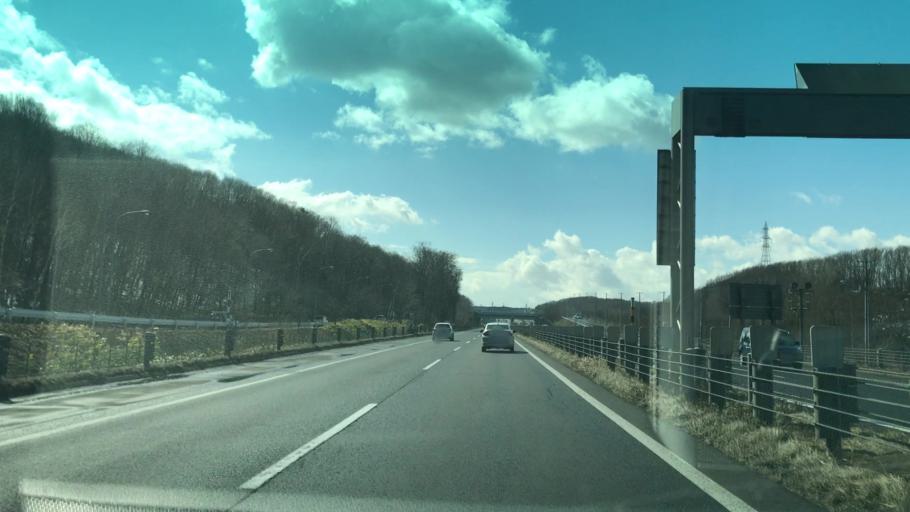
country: JP
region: Hokkaido
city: Kitahiroshima
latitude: 43.0061
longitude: 141.4669
